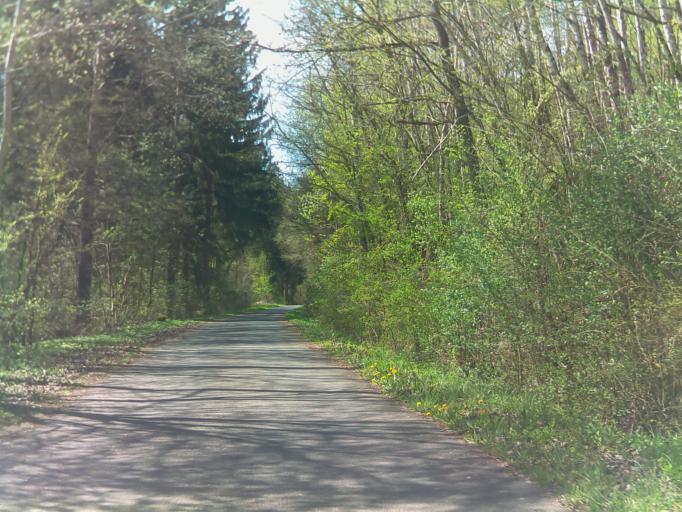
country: DE
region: Thuringia
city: Hellingen
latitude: 50.2869
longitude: 10.7808
